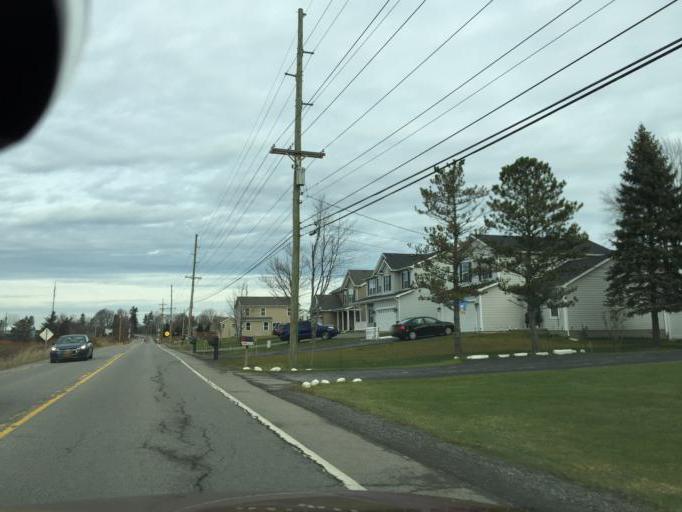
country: US
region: New York
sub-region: Monroe County
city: Scottsville
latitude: 43.0976
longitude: -77.7327
